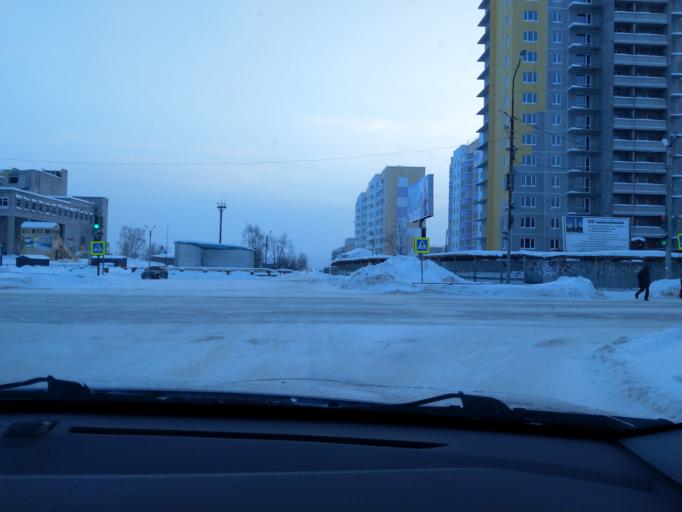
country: RU
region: Perm
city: Dobryanka
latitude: 58.4631
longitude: 56.4000
